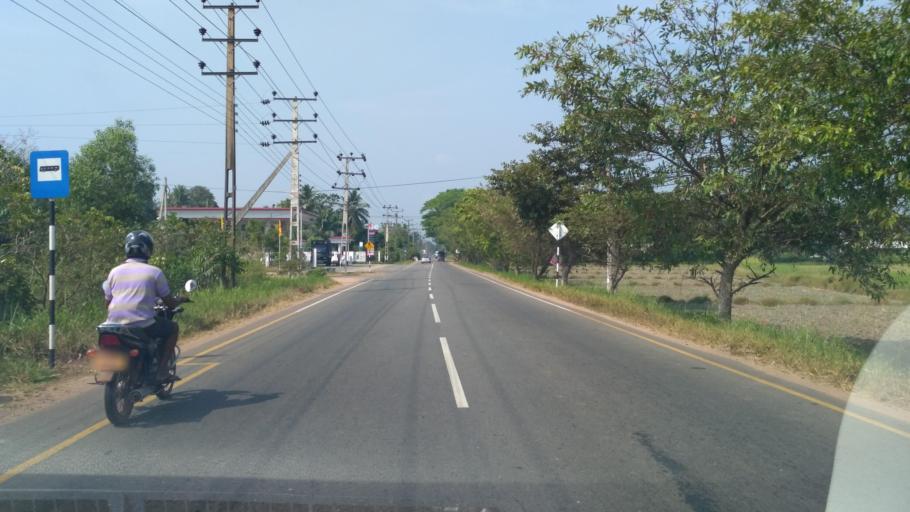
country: LK
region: North Western
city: Kuliyapitiya
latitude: 7.3260
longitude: 79.9884
